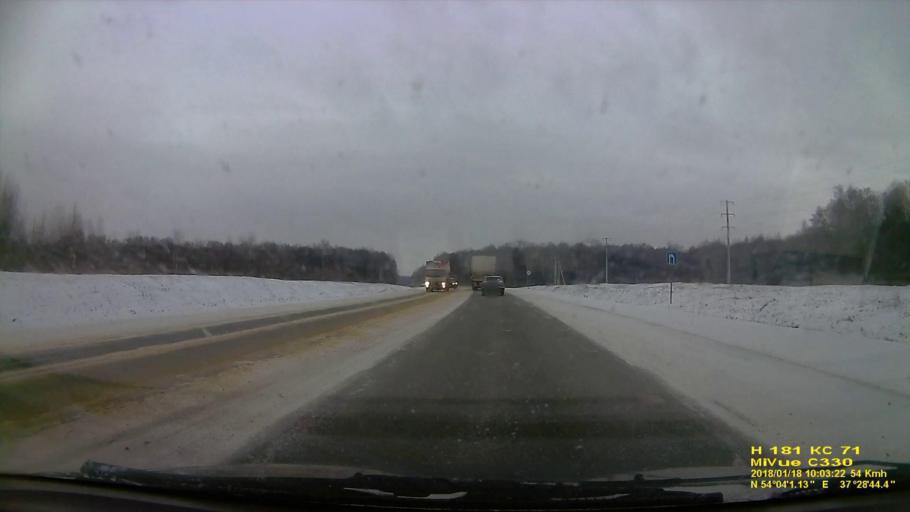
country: RU
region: Tula
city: Pervomayskiy
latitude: 54.0668
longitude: 37.4791
